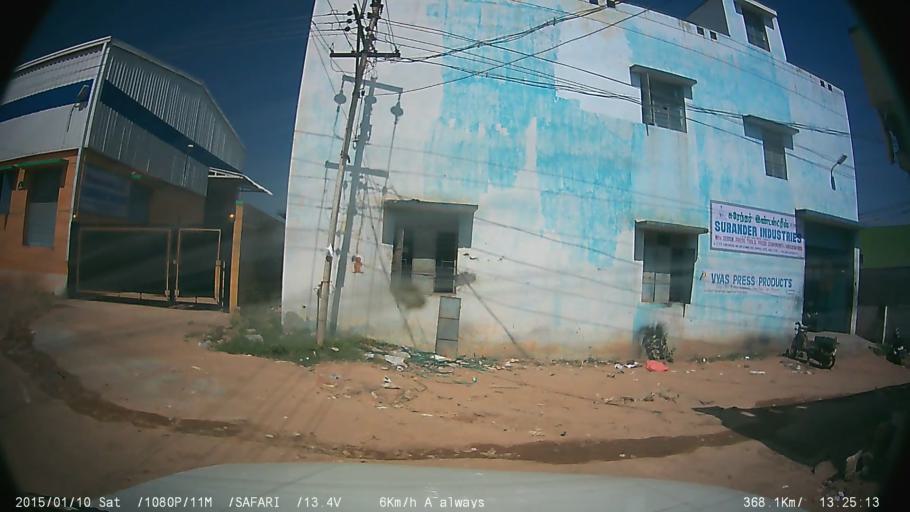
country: IN
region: Tamil Nadu
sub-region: Krishnagiri
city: Hosur
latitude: 12.7760
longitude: 77.7973
